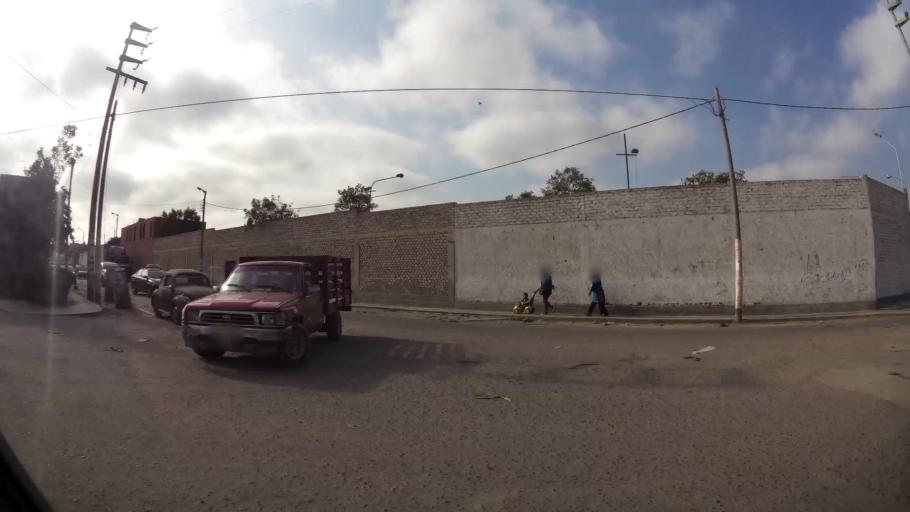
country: PE
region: La Libertad
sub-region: Provincia de Trujillo
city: El Porvenir
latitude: -8.0924
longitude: -79.0220
